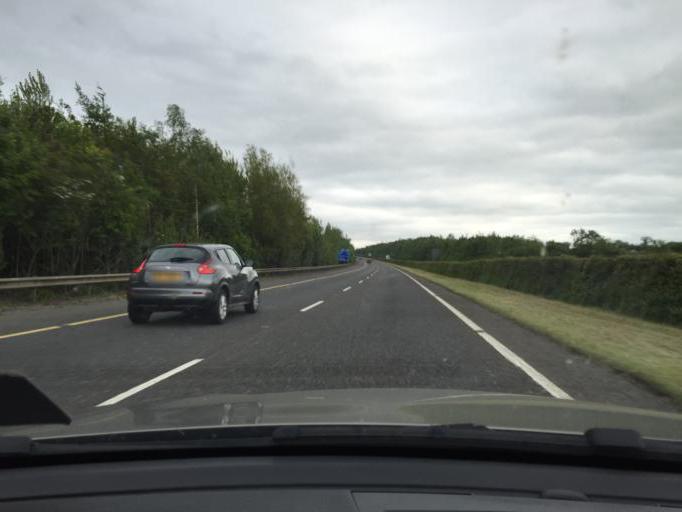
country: IE
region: Leinster
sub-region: An Mhi
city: Stamullin
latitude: 53.6289
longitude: -6.2496
